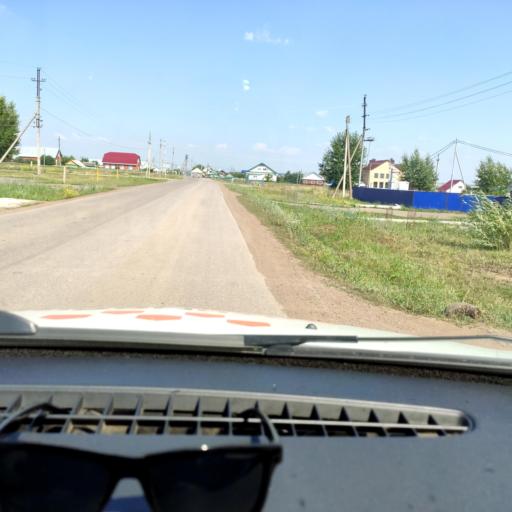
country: RU
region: Bashkortostan
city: Chekmagush
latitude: 55.1429
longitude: 54.6230
